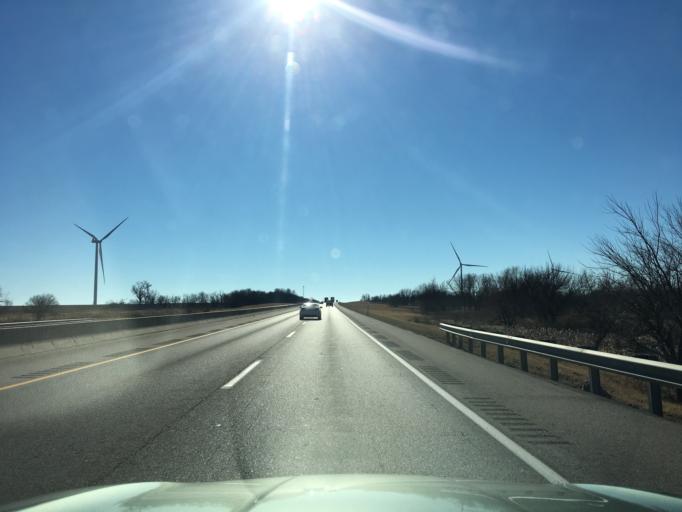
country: US
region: Kansas
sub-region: Sumner County
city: Wellington
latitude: 37.1338
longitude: -97.3391
